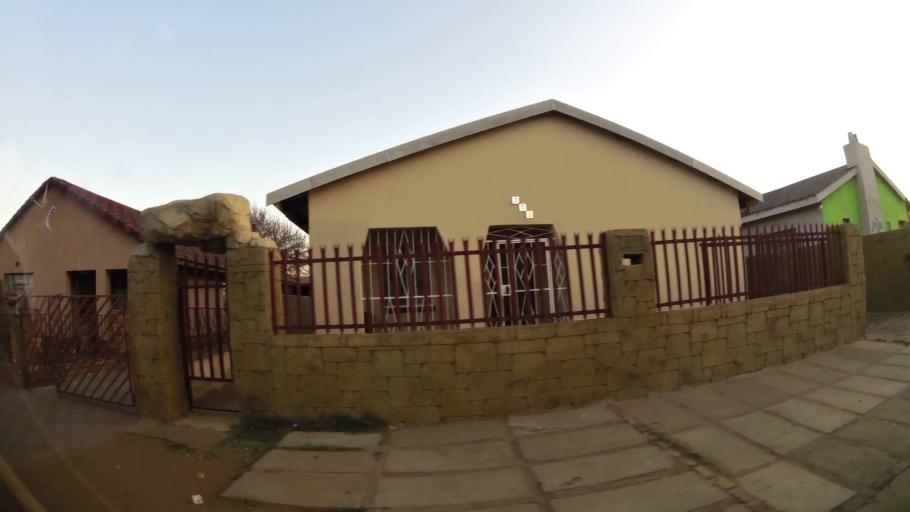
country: ZA
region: Gauteng
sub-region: West Rand District Municipality
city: Randfontein
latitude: -26.2023
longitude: 27.7120
